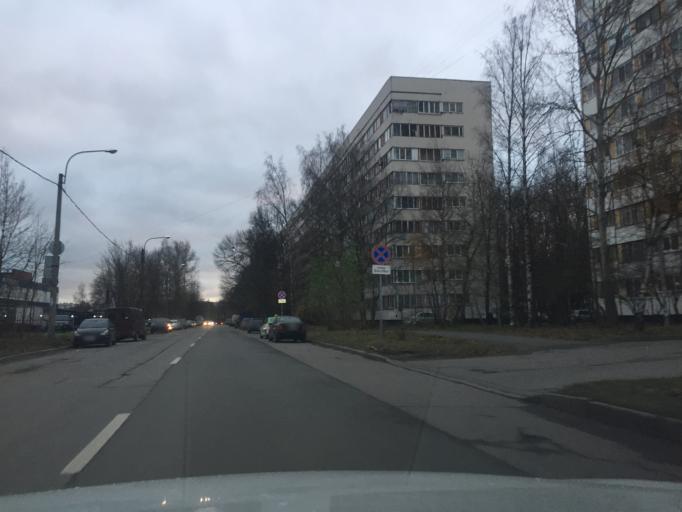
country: RU
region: St.-Petersburg
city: Grazhdanka
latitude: 60.0245
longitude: 30.4284
